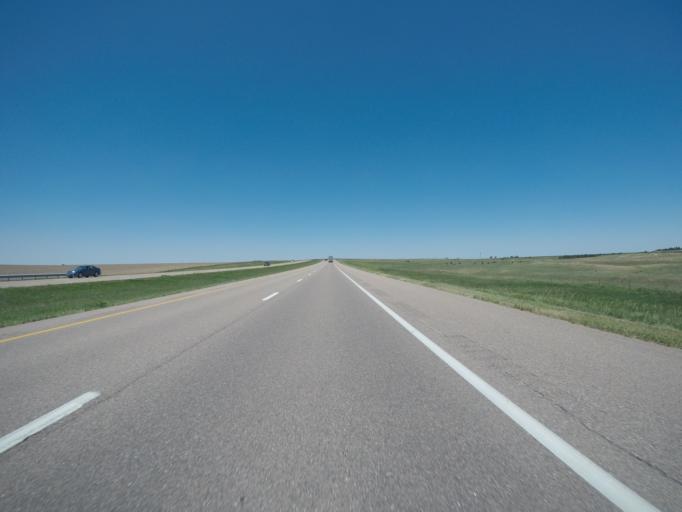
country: US
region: Kansas
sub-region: Gove County
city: Gove
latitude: 39.0717
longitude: -100.2707
